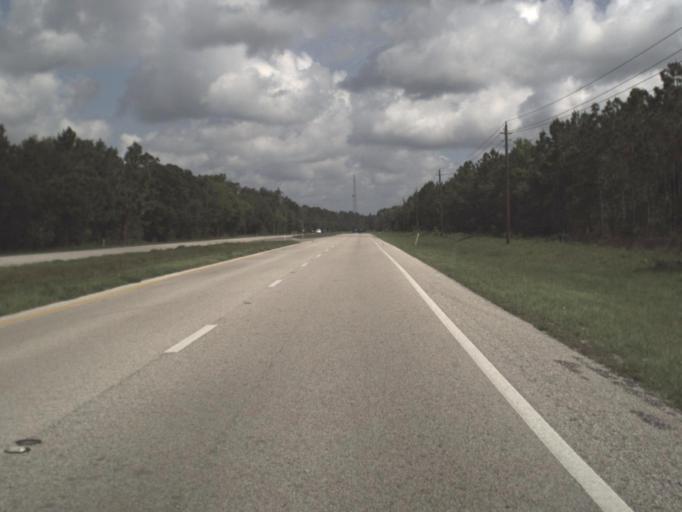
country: US
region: Florida
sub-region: Flagler County
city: Palm Coast
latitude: 29.6734
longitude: -81.2907
